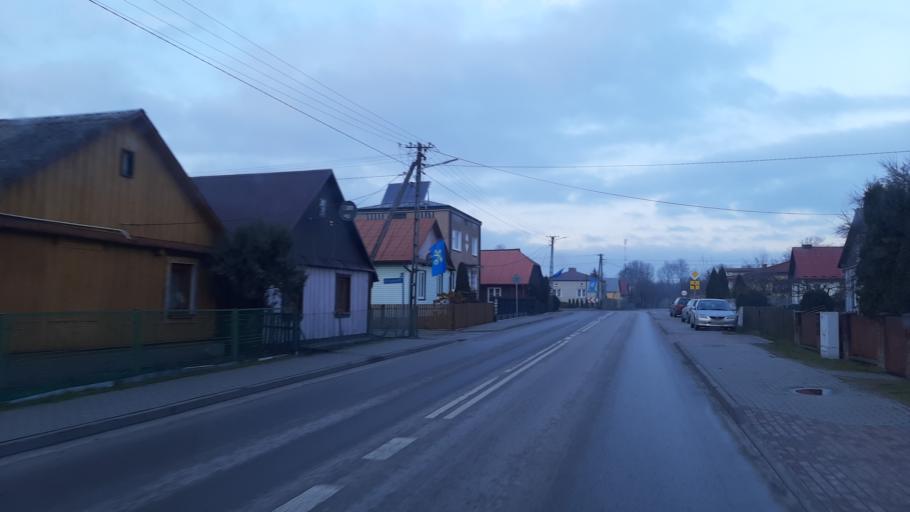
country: PL
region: Lublin Voivodeship
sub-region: Powiat lubartowski
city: Kamionka
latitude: 51.4714
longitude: 22.4627
